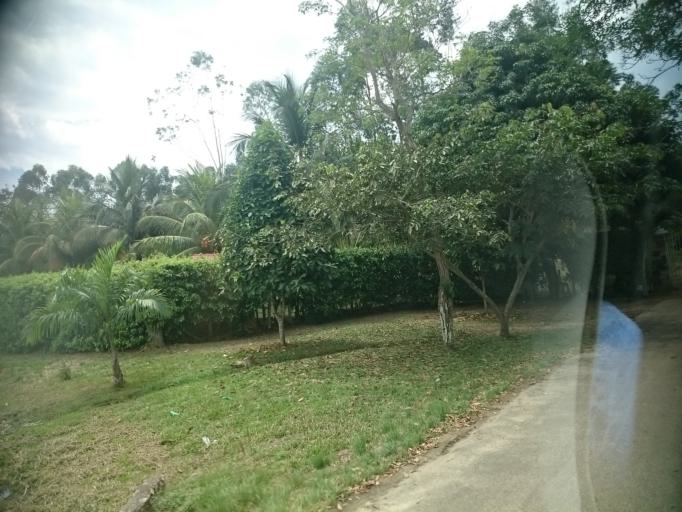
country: PE
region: San Martin
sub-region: Provincia de San Martin
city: Tarapoto
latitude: -6.5120
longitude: -76.3443
